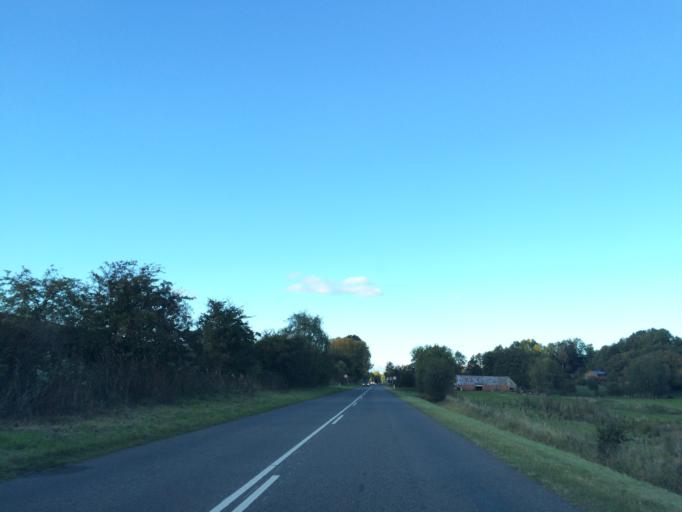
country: DK
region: Central Jutland
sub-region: Skanderborg Kommune
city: Ry
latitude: 56.1079
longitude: 9.7343
